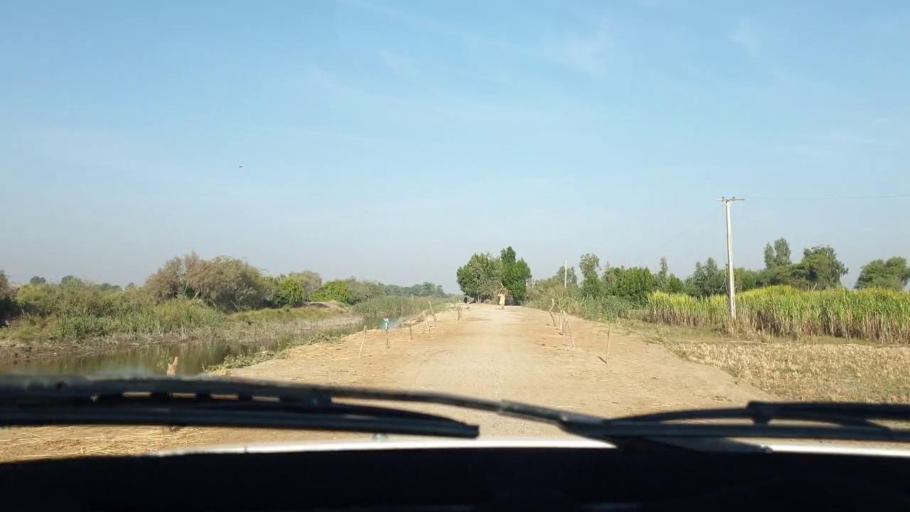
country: PK
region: Sindh
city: Tando Muhammad Khan
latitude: 25.0245
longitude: 68.4863
